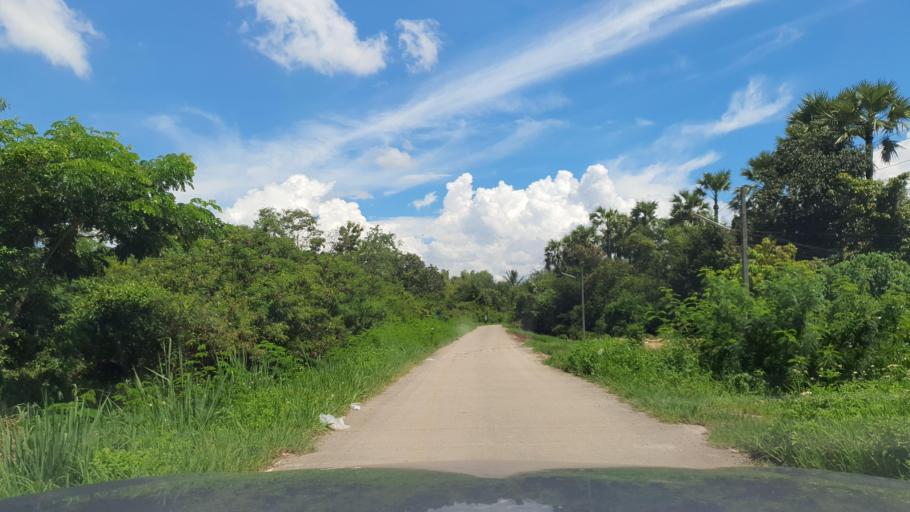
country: TH
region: Chiang Mai
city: San Kamphaeng
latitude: 18.7328
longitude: 99.1191
